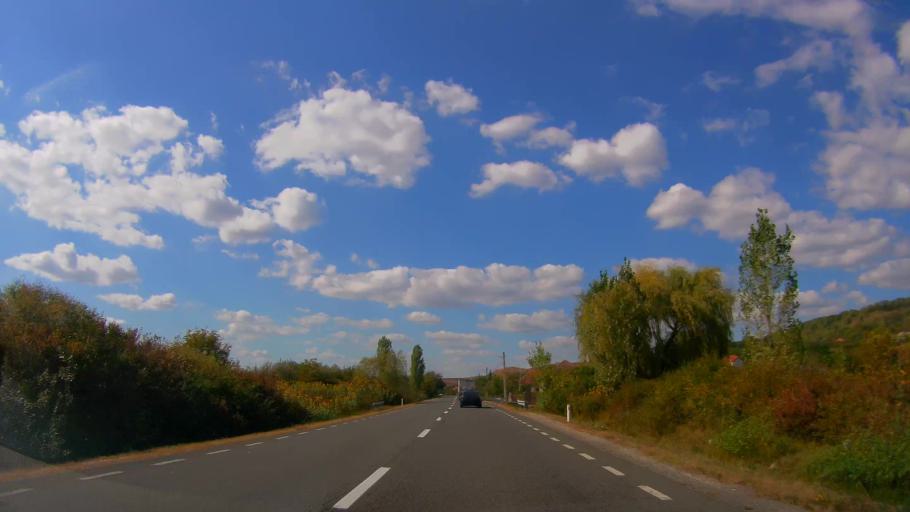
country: RO
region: Salaj
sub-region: Comuna Bocsa
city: Bocsa
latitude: 47.3149
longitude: 22.9106
